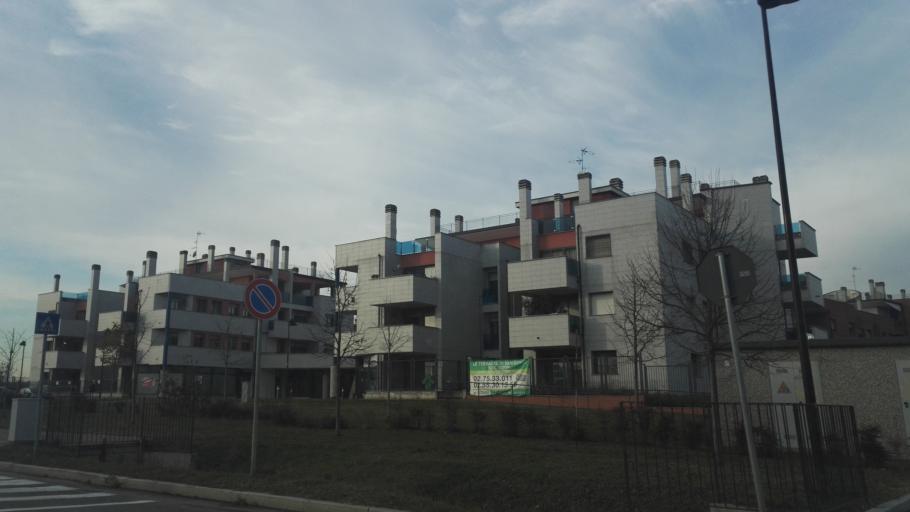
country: IT
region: Lombardy
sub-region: Citta metropolitana di Milano
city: San Bovio-San Felice
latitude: 45.4633
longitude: 9.3072
